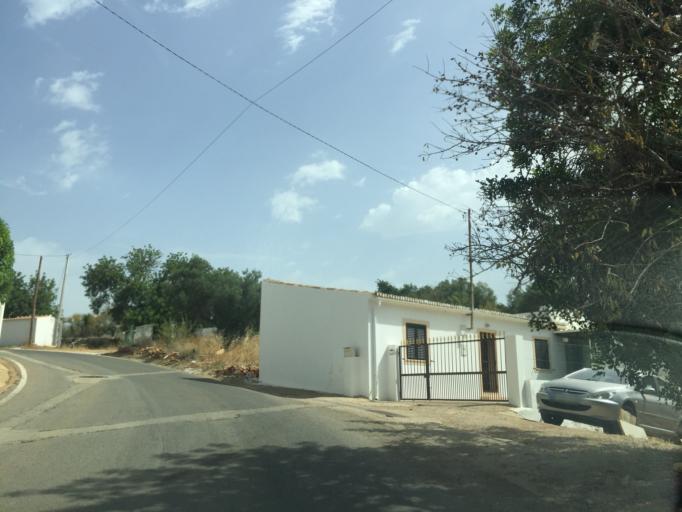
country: PT
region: Faro
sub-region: Loule
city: Boliqueime
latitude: 37.1271
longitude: -8.1423
